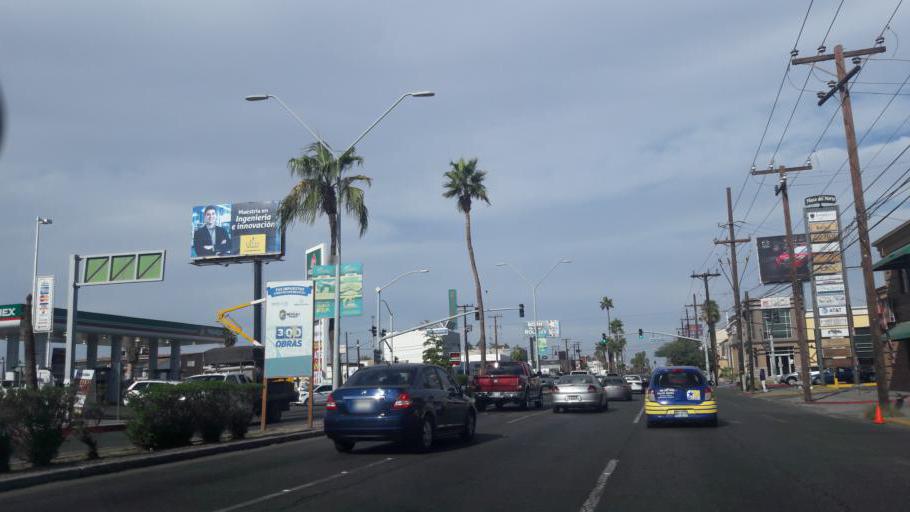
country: MX
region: Baja California
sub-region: Mexicali
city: Mexicali
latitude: 32.6526
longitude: -115.4524
